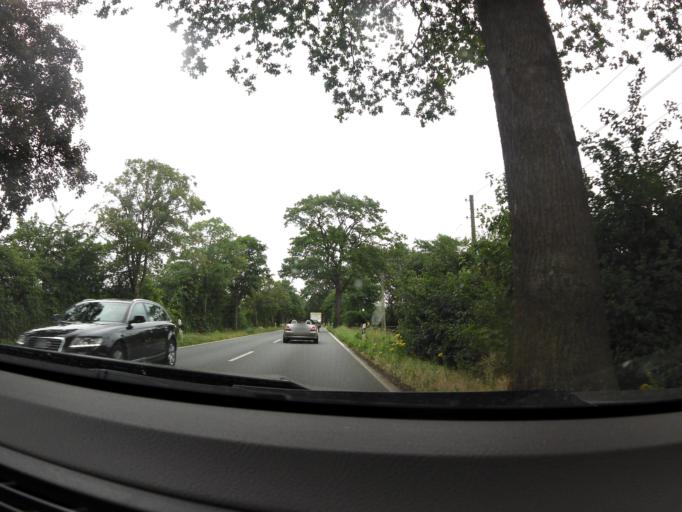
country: DE
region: North Rhine-Westphalia
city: Straelen
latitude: 51.4800
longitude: 6.2923
